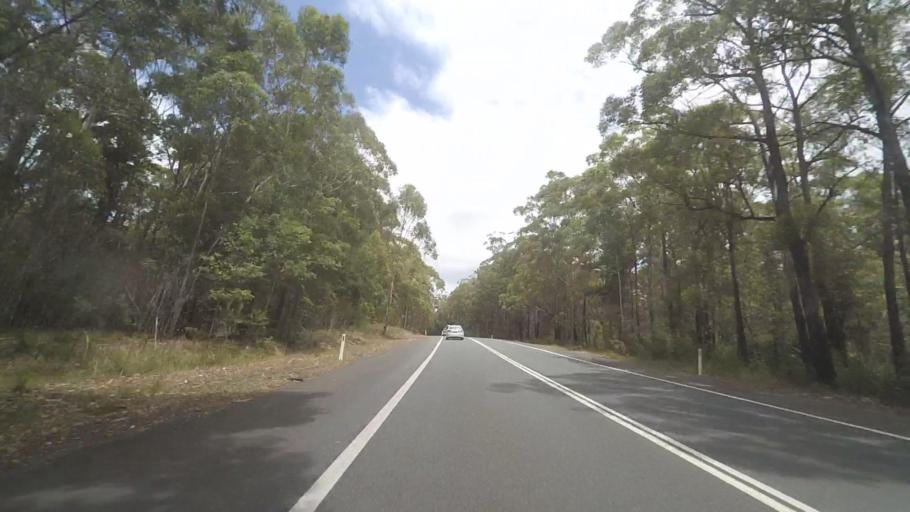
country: AU
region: New South Wales
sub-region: Shoalhaven Shire
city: Milton
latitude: -35.1574
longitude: 150.4494
